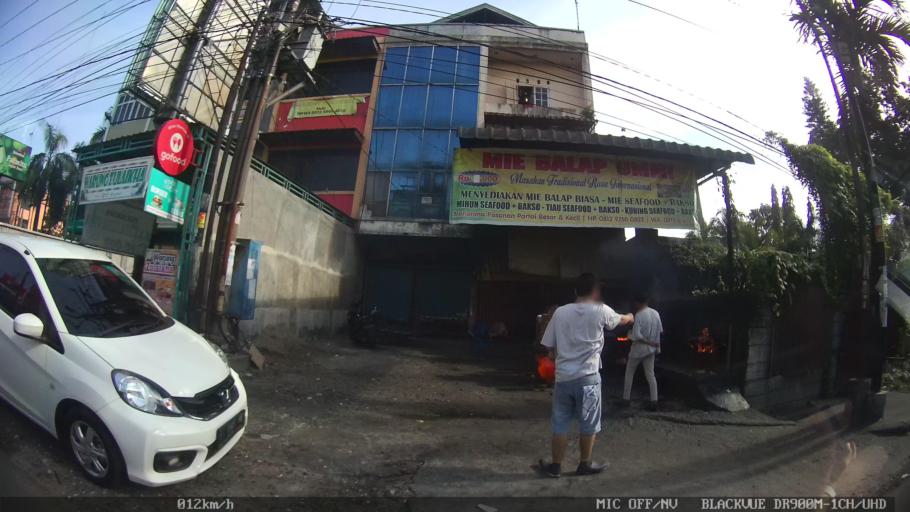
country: ID
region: North Sumatra
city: Medan
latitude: 3.6047
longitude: 98.6460
